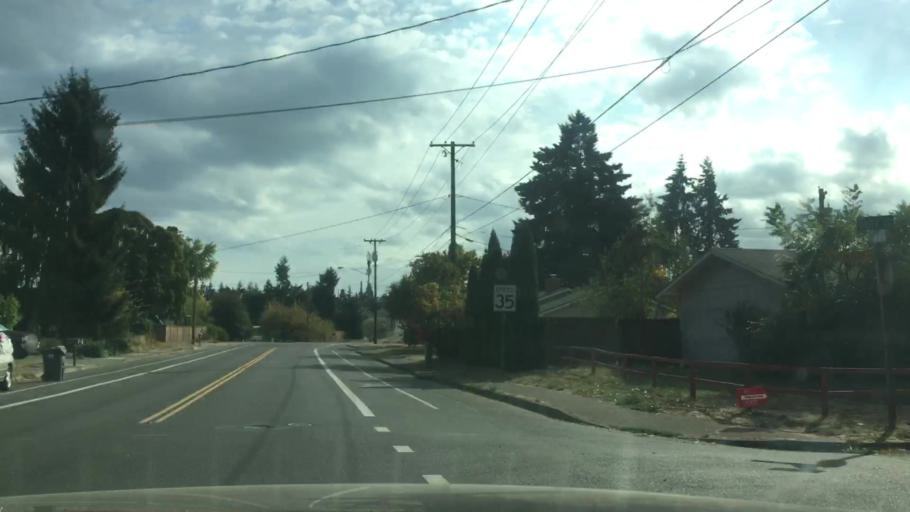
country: US
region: Oregon
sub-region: Lane County
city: Eugene
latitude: 44.0918
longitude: -123.0877
